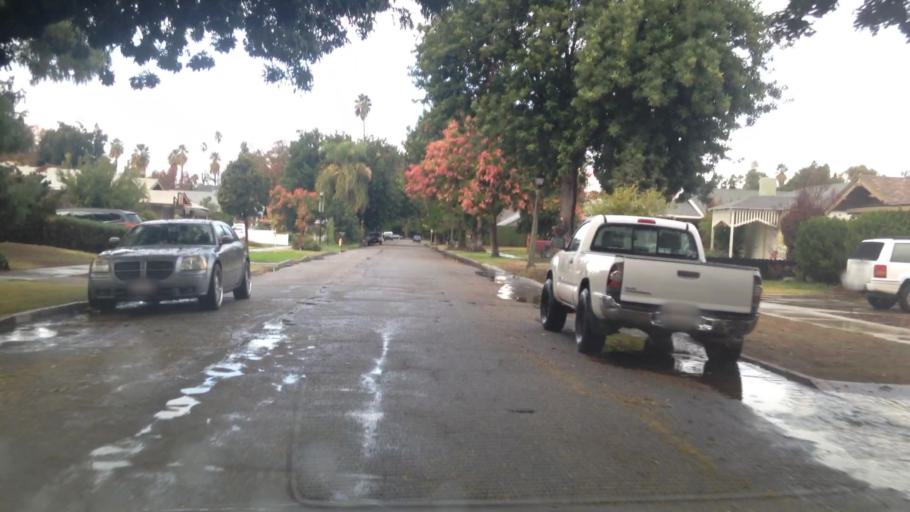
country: US
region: California
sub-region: Riverside County
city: Riverside
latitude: 33.9413
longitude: -117.4045
